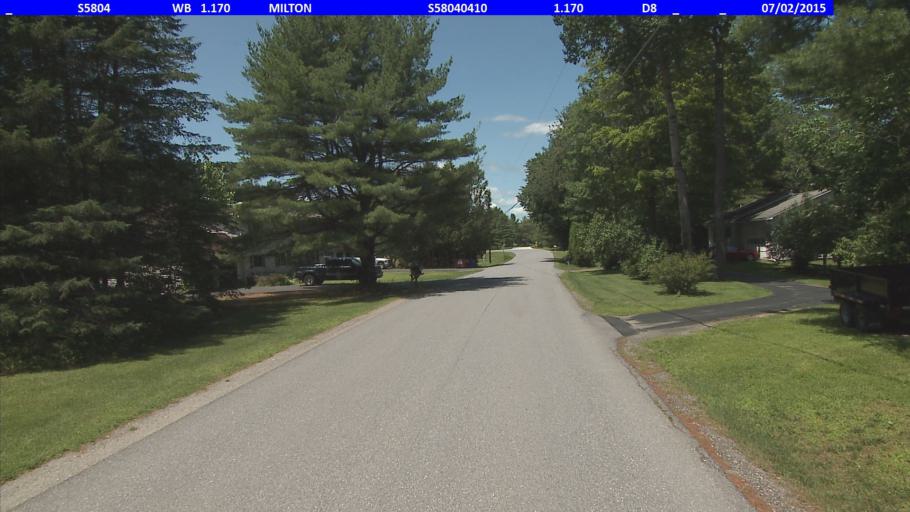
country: US
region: Vermont
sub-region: Chittenden County
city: Milton
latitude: 44.6567
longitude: -73.1508
